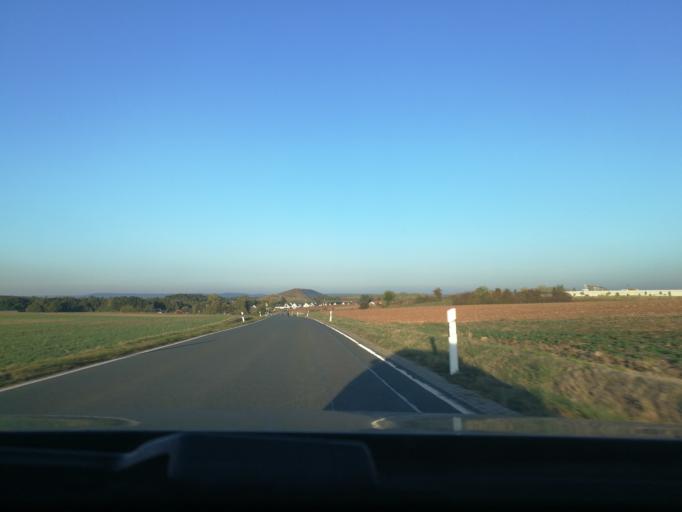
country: DE
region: Bavaria
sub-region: Regierungsbezirk Mittelfranken
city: Obermichelbach
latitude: 49.5015
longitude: 10.9393
